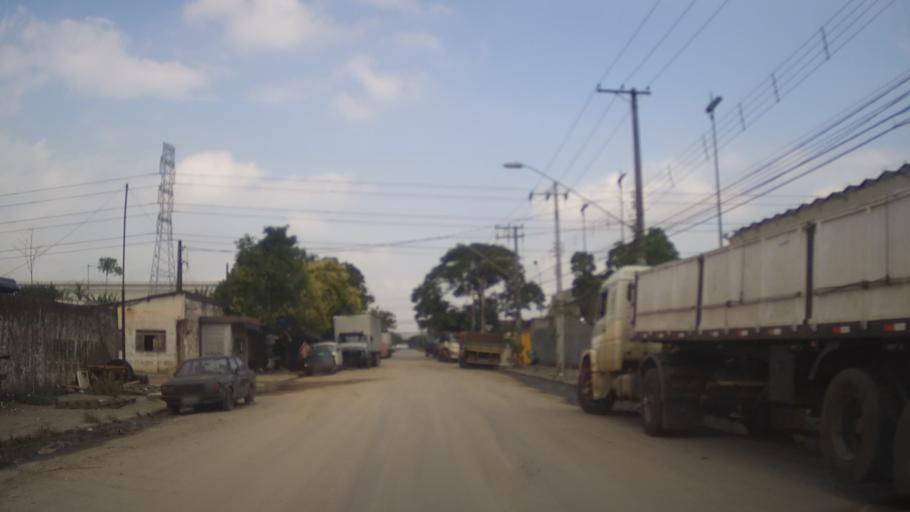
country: BR
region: Sao Paulo
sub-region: Guarulhos
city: Guarulhos
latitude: -23.4727
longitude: -46.4739
